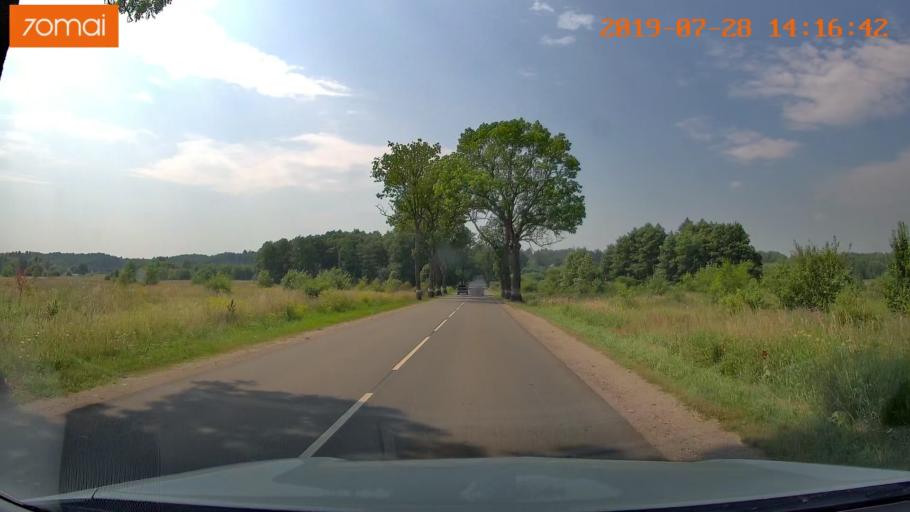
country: RU
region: Kaliningrad
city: Vzmorye
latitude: 54.8159
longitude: 20.2652
